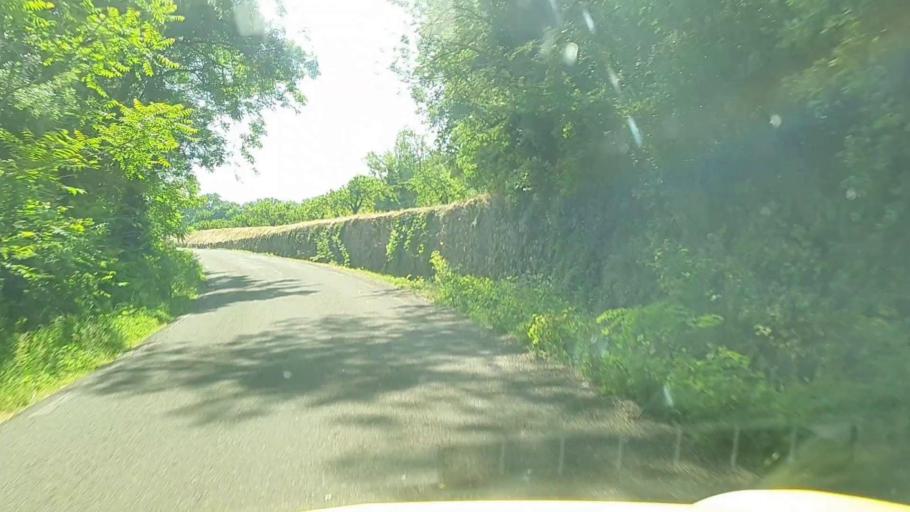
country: FR
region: Languedoc-Roussillon
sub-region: Departement du Gard
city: Tresques
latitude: 44.0937
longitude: 4.5574
